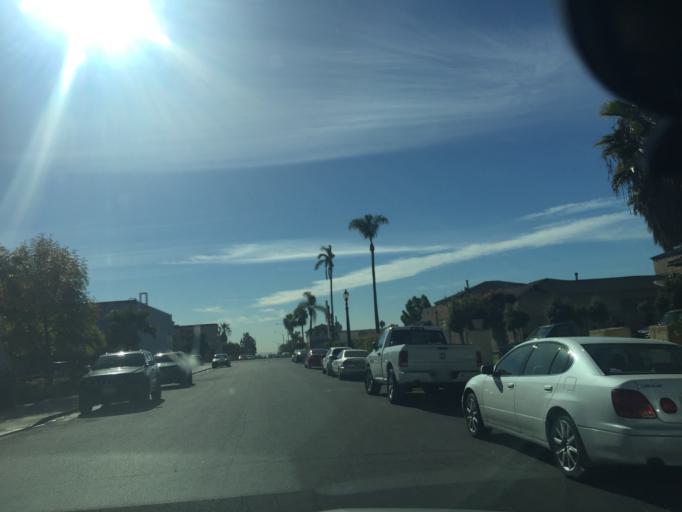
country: US
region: California
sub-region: San Diego County
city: Lemon Grove
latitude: 32.7578
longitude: -117.0869
